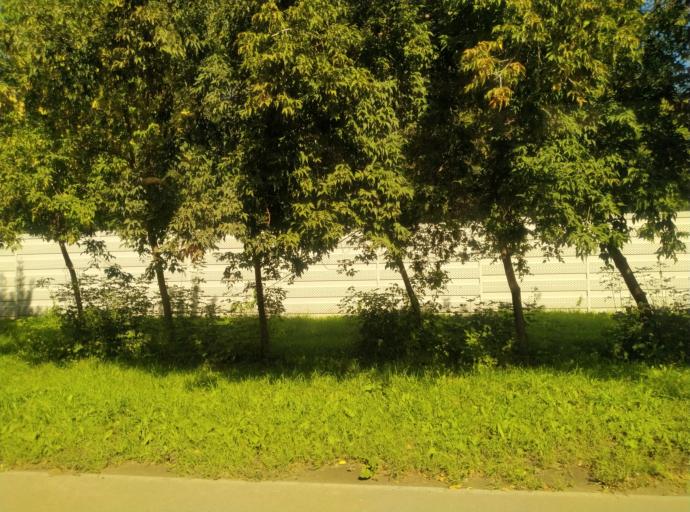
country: RU
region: Krasnoyarskiy
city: Krasnoyarsk
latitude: 55.9779
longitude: 92.8321
